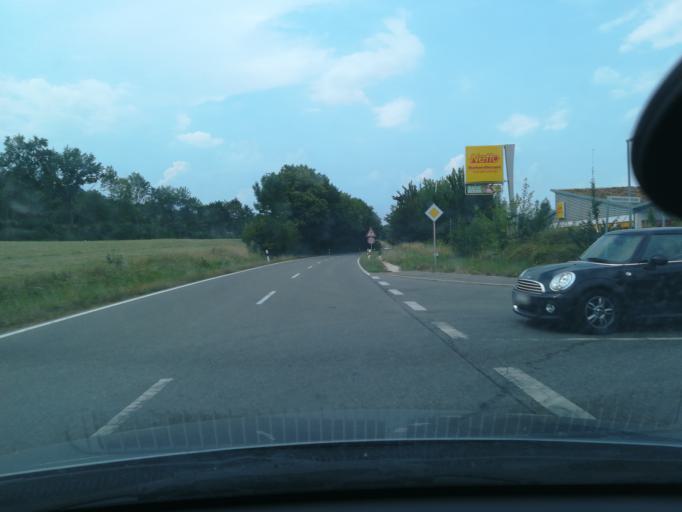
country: DE
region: Baden-Wuerttemberg
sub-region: Freiburg Region
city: Muhlhausen-Ehingen
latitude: 47.8016
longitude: 8.8233
